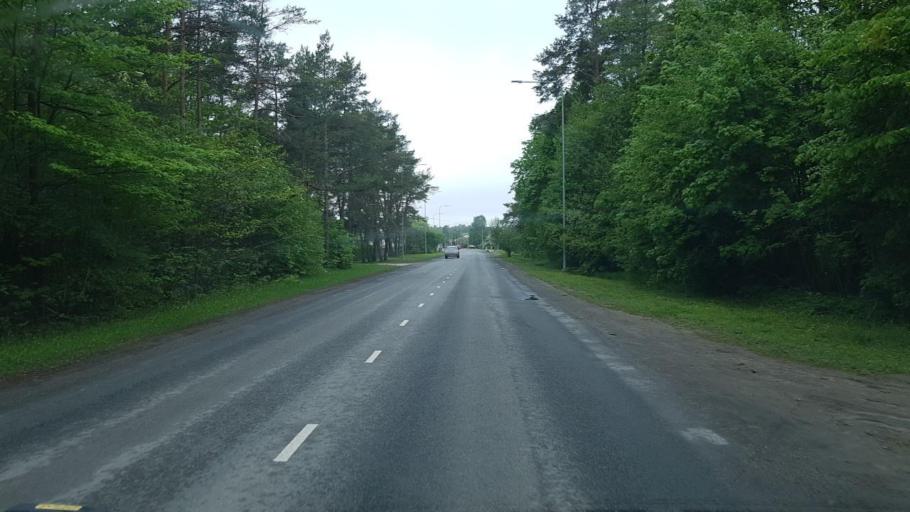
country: EE
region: Laeaene
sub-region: Haapsalu linn
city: Haapsalu
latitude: 58.9289
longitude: 23.5353
